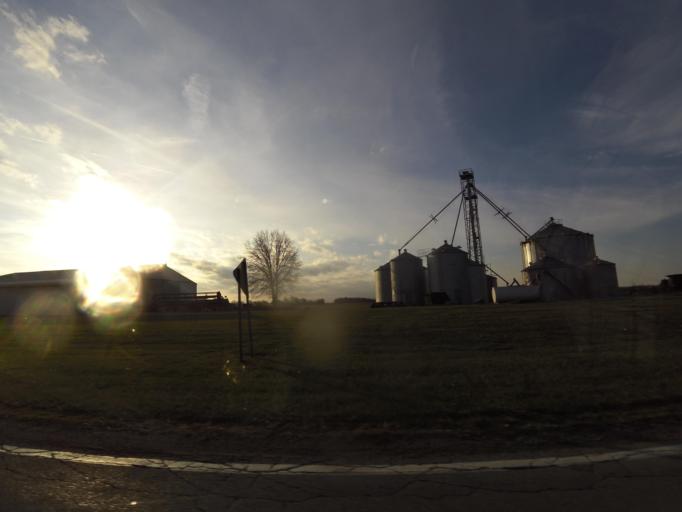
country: US
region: Illinois
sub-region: Fayette County
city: Vandalia
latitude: 38.9207
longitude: -89.2191
